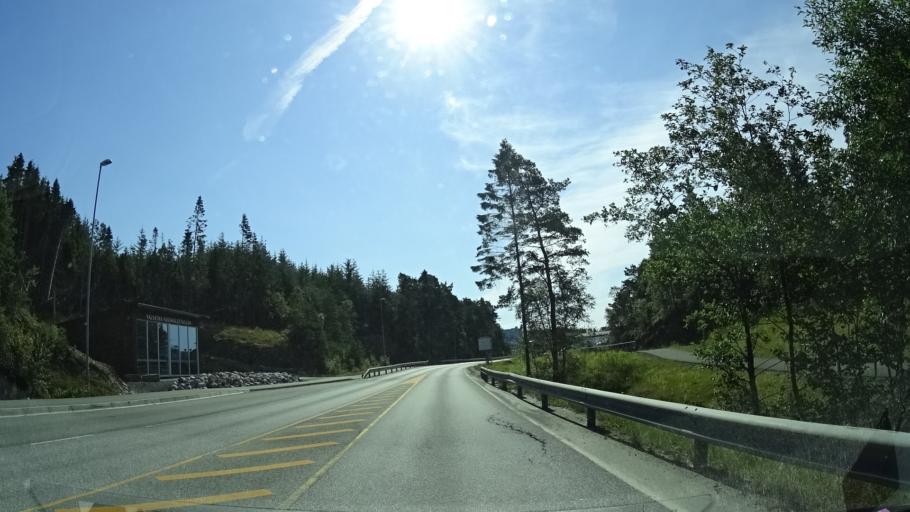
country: NO
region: Hordaland
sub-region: Stord
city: Sagvag
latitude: 59.7658
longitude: 5.4449
